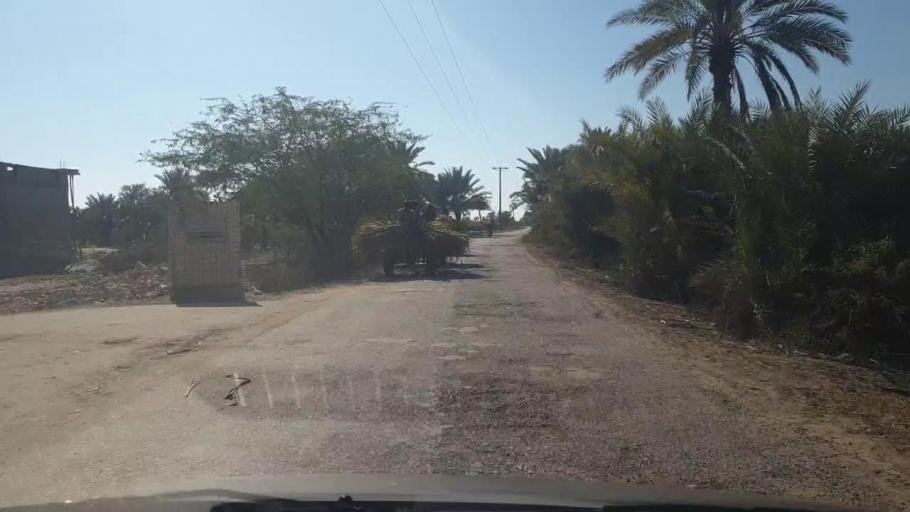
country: PK
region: Sindh
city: Bozdar
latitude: 27.2439
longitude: 68.6521
